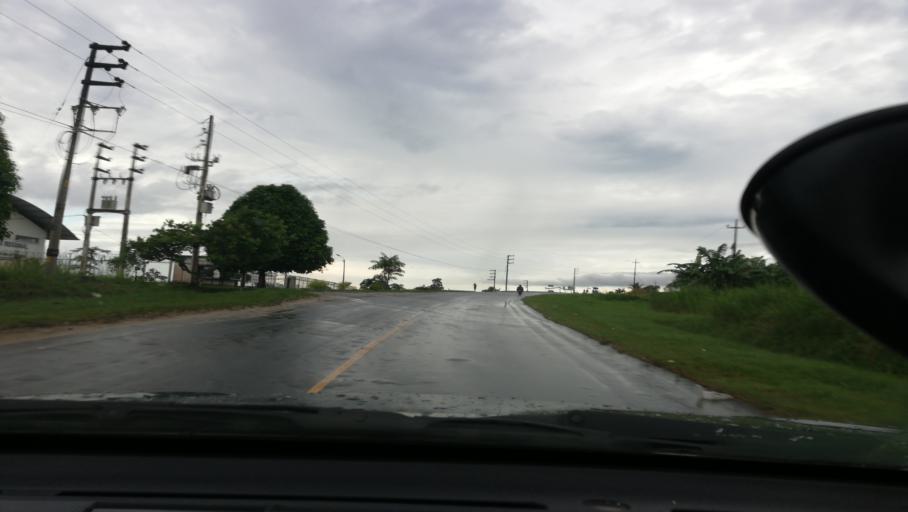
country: PE
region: Loreto
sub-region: Provincia de Maynas
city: Iquitos
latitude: -3.8539
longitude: -73.3379
